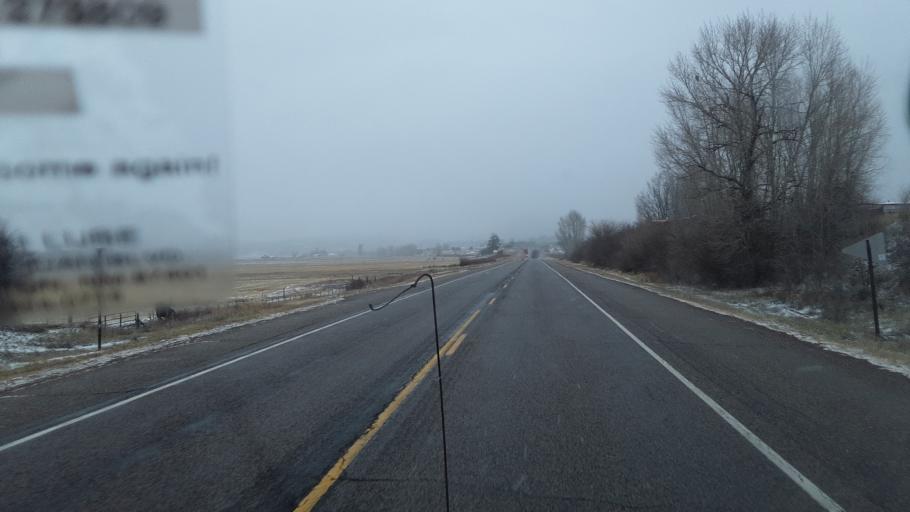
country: US
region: New Mexico
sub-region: Rio Arriba County
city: Tierra Amarilla
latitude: 36.7506
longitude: -106.5645
